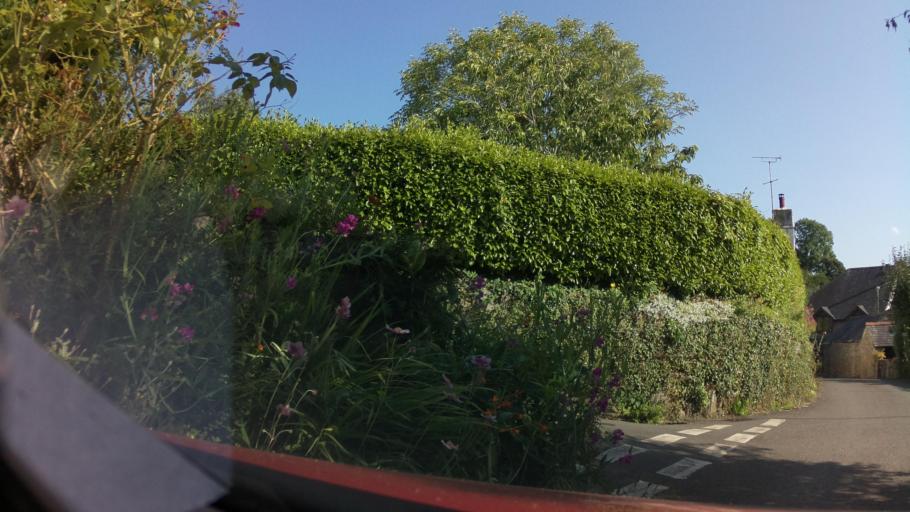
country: GB
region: England
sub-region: Devon
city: Totnes
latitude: 50.4140
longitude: -3.7225
